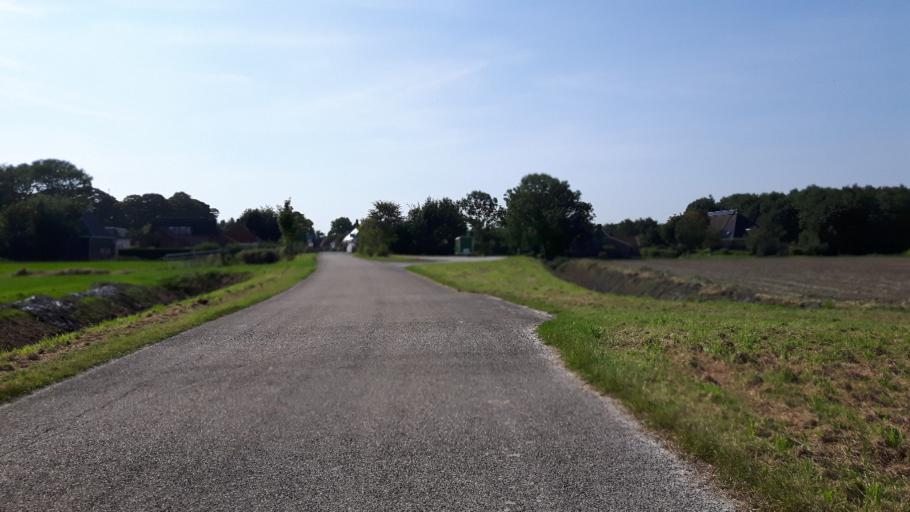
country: NL
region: Friesland
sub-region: Gemeente Ferwerderadiel
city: Hallum
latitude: 53.2942
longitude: 5.7685
